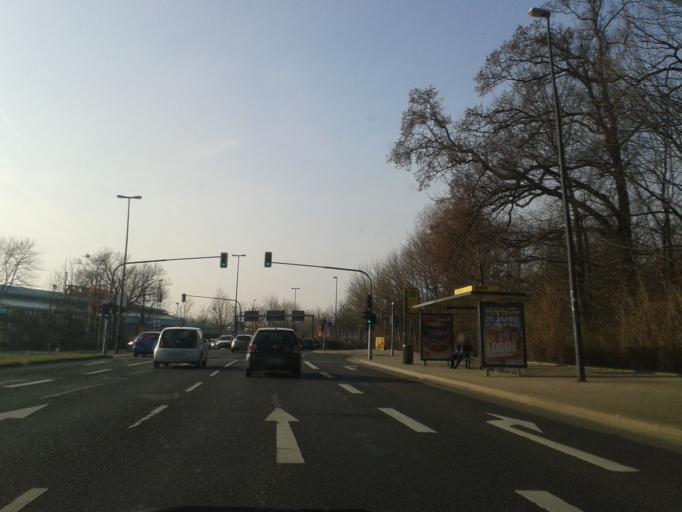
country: DE
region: Saxony
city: Dresden
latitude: 51.0054
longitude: 13.7888
